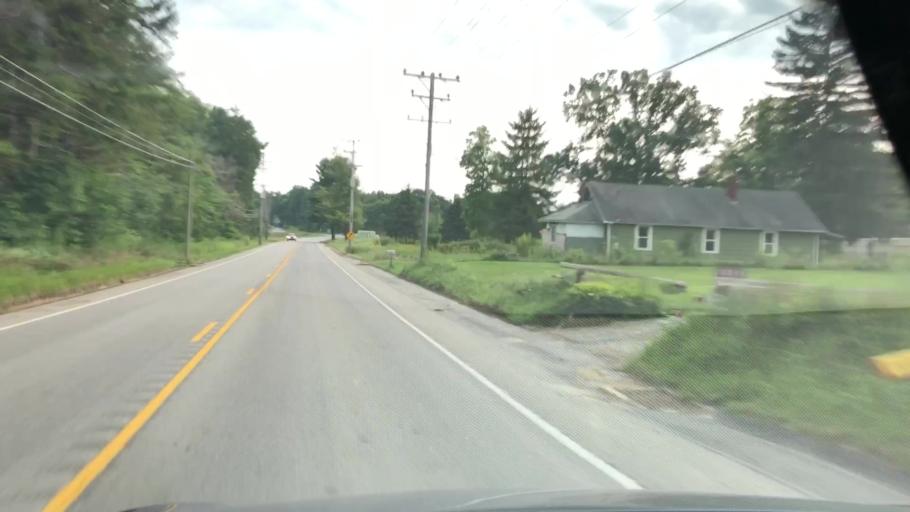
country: US
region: Pennsylvania
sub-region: Crawford County
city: Titusville
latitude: 41.5470
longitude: -79.7038
